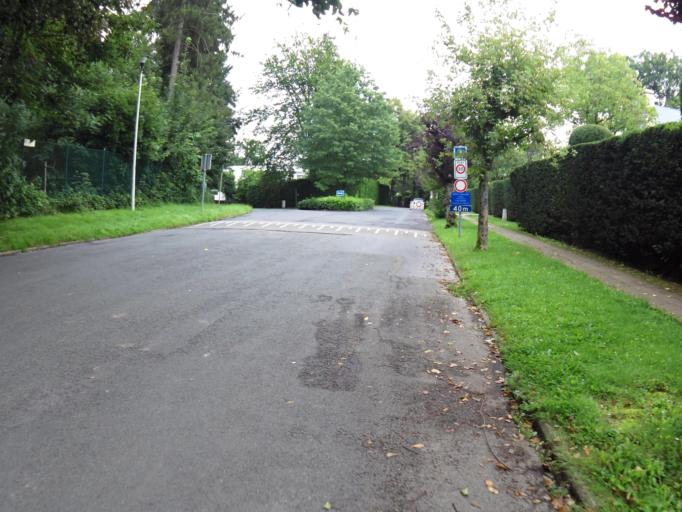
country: BE
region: Flanders
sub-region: Provincie Vlaams-Brabant
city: Kraainem
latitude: 50.8227
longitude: 4.4373
